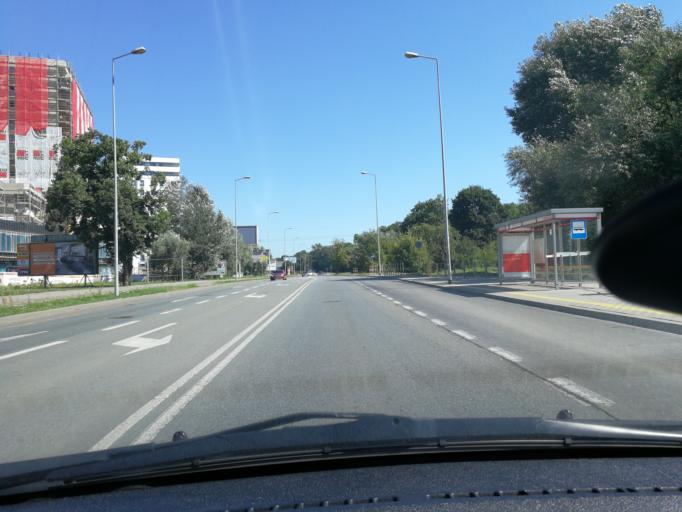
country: PL
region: Masovian Voivodeship
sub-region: Warszawa
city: Targowek
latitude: 52.2971
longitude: 21.0556
